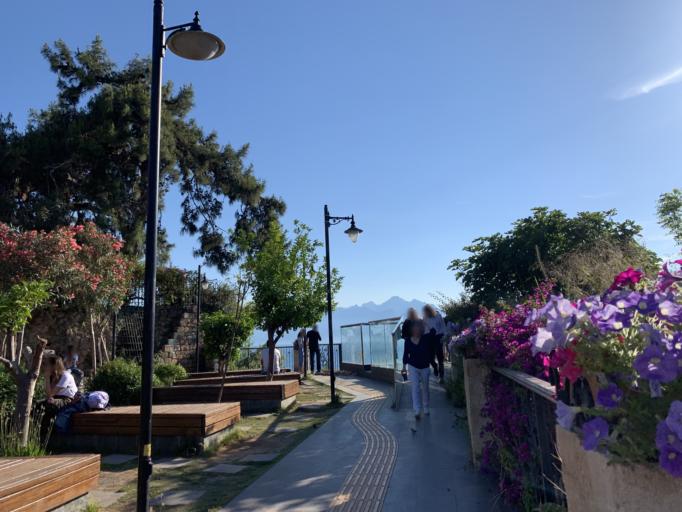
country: TR
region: Antalya
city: Antalya
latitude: 36.8829
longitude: 30.7033
